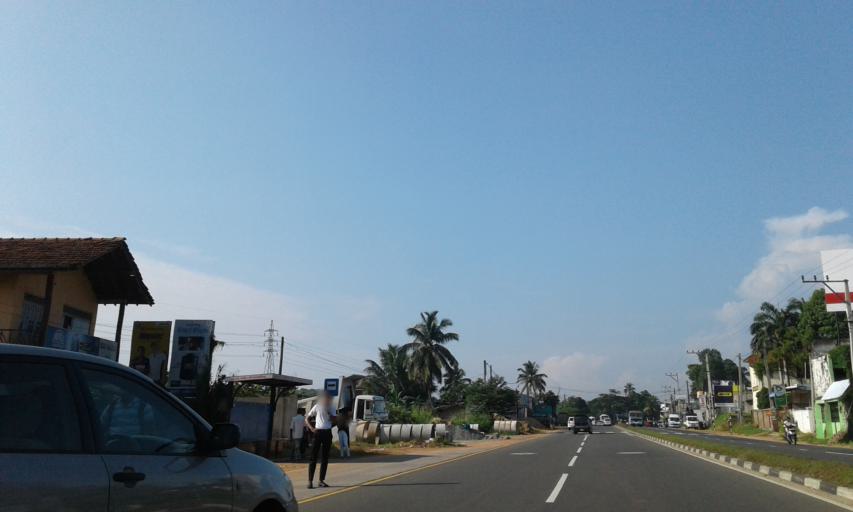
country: LK
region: Western
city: Gampaha
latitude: 7.0491
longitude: 80.0012
